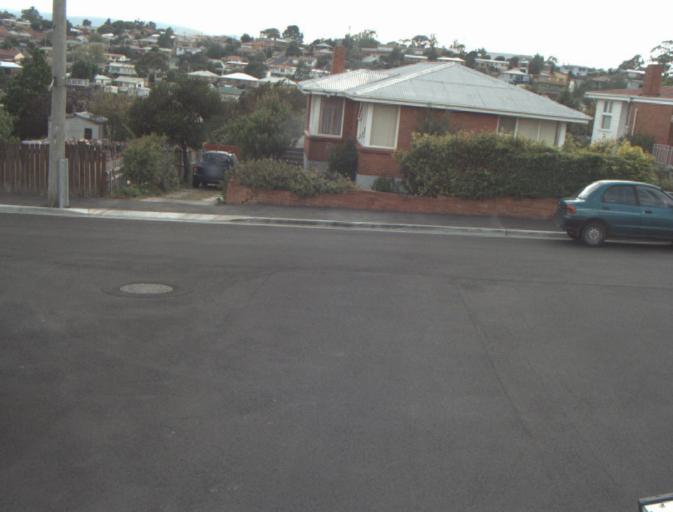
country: AU
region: Tasmania
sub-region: Launceston
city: Summerhill
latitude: -41.4797
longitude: 147.1644
